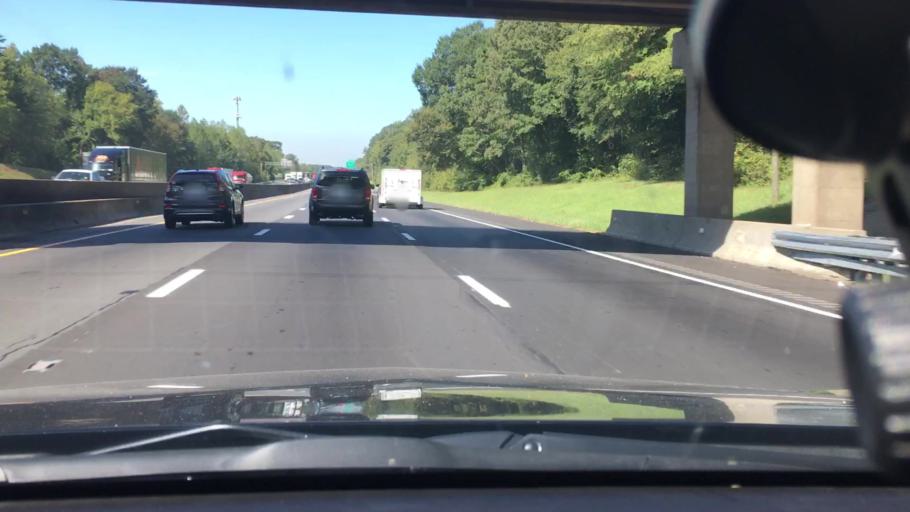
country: US
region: North Carolina
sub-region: Gaston County
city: Lowell
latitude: 35.2611
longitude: -81.1091
